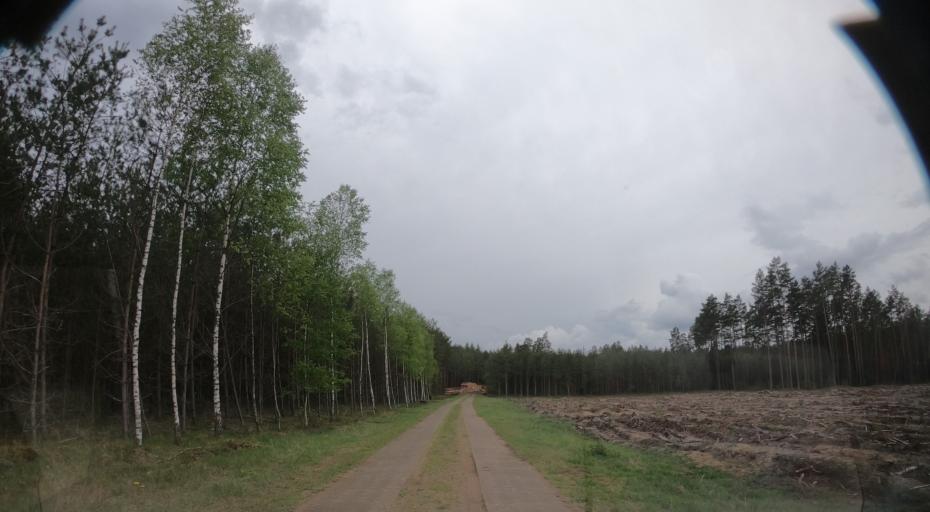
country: PL
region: West Pomeranian Voivodeship
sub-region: Powiat koszalinski
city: Bobolice
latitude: 54.0633
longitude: 16.4244
